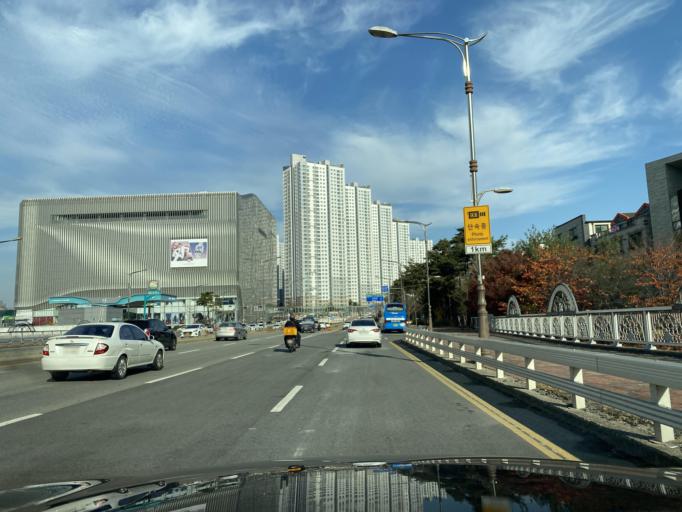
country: KR
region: Chungcheongnam-do
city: Cheonan
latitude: 36.7988
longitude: 127.1062
